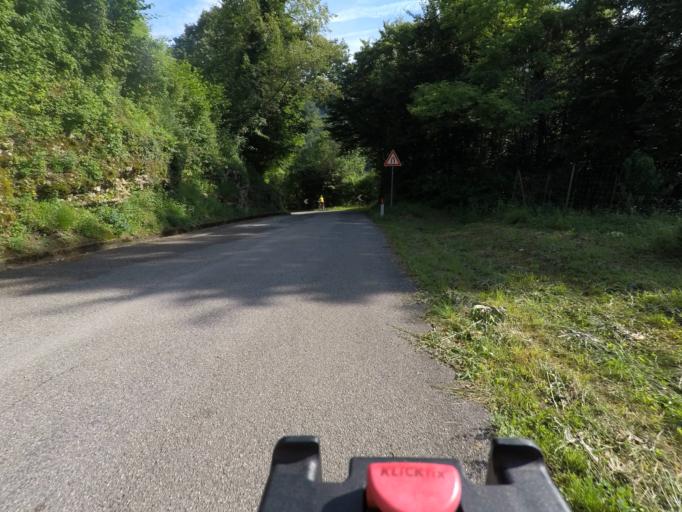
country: IT
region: Friuli Venezia Giulia
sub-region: Provincia di Udine
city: Pulfero
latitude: 46.1688
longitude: 13.4848
